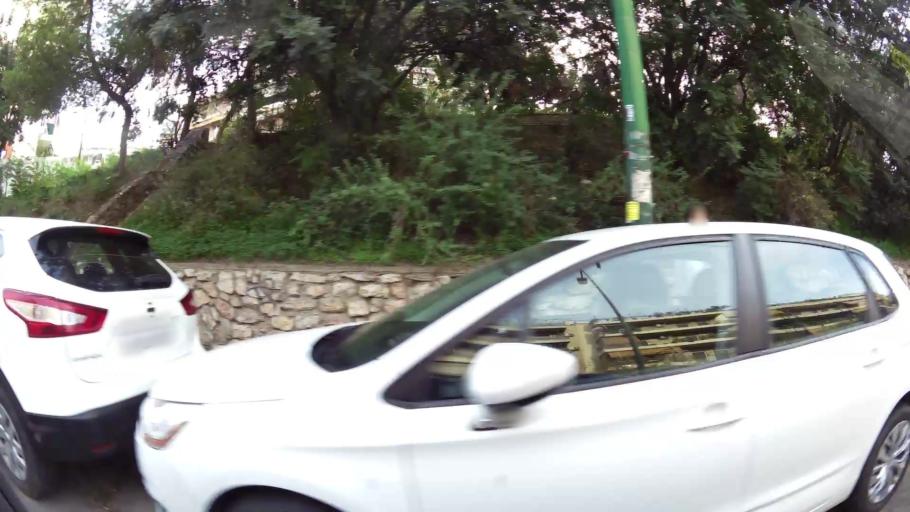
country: GR
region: Attica
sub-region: Nomarchia Athinas
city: Nea Chalkidona
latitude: 38.0247
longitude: 23.7310
